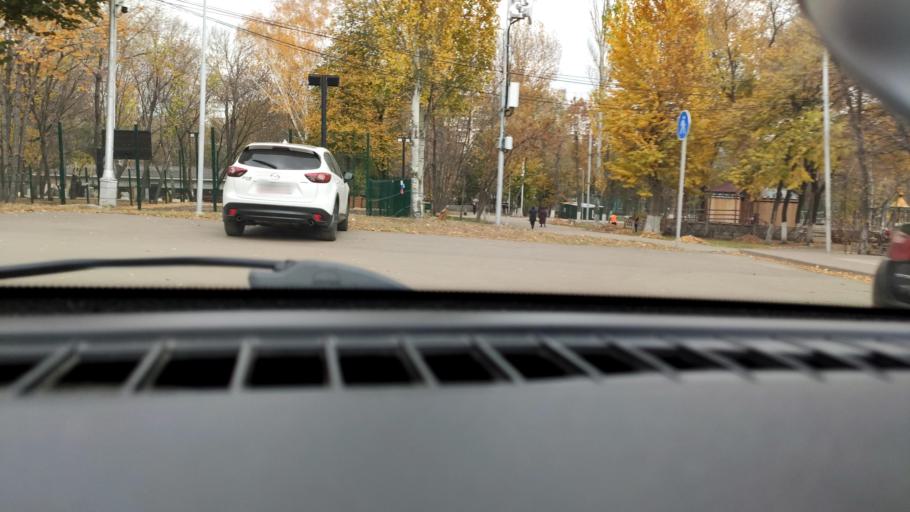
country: RU
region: Samara
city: Samara
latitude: 53.2032
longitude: 50.2188
